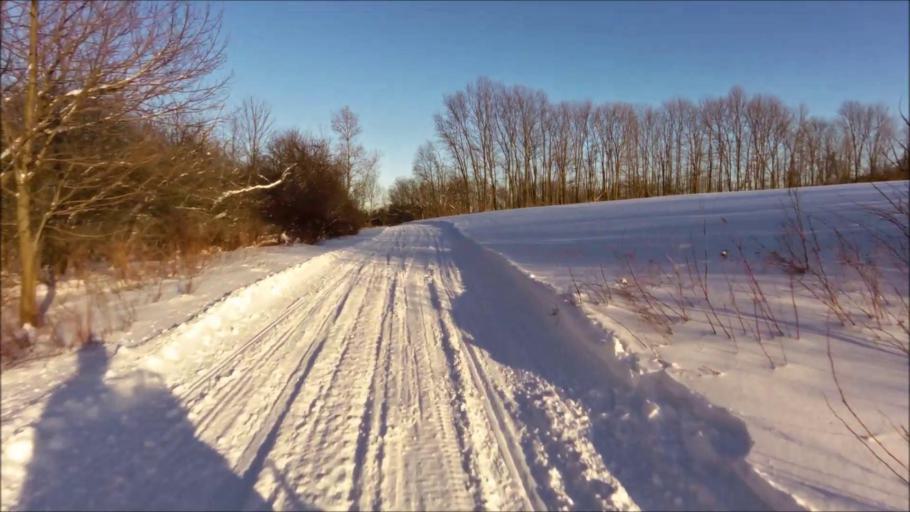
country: US
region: New York
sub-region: Chautauqua County
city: Celoron
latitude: 42.2268
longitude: -79.3150
